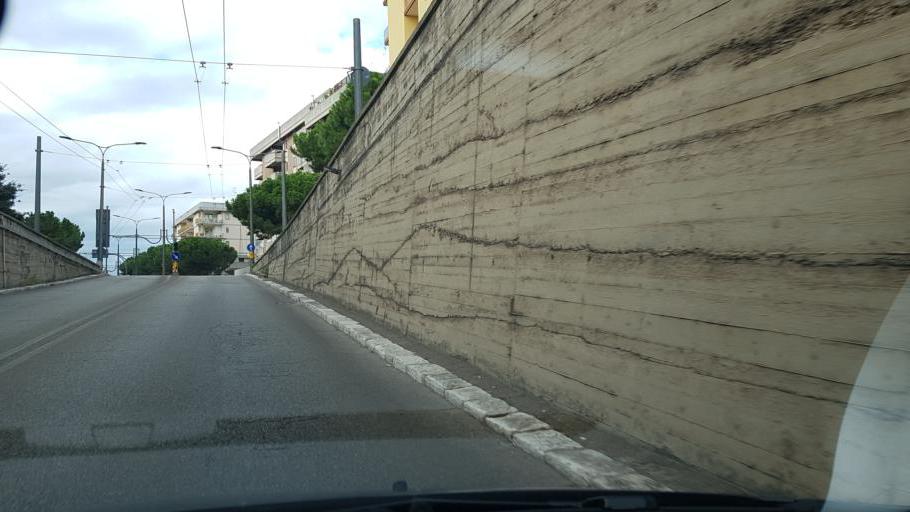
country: IT
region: Apulia
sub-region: Provincia di Lecce
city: Lecce
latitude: 40.3568
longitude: 18.1842
